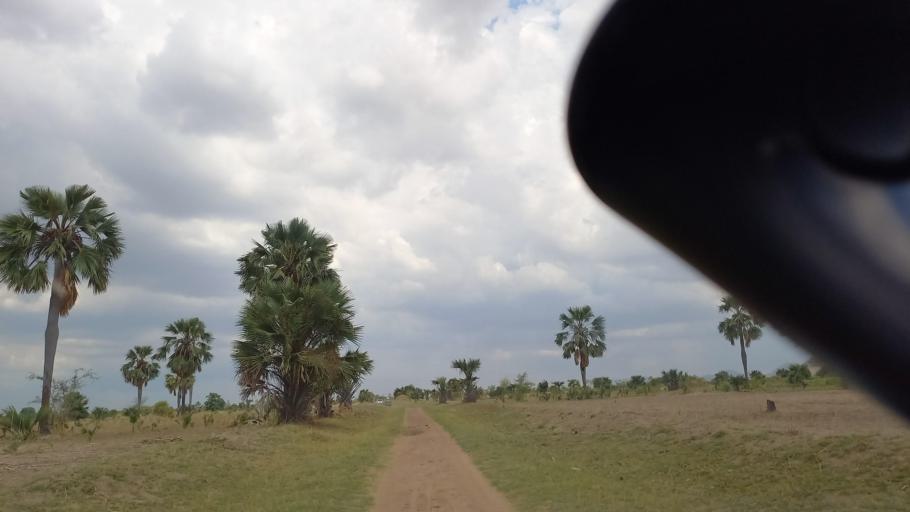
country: ZM
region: Lusaka
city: Kafue
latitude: -15.8281
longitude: 28.0568
